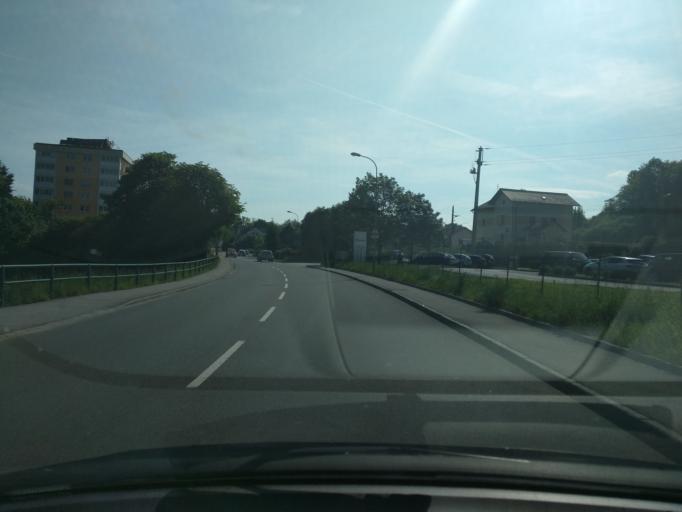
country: AT
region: Lower Austria
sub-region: Politischer Bezirk Amstetten
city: Kematen an der Ybbs
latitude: 48.0228
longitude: 14.7601
